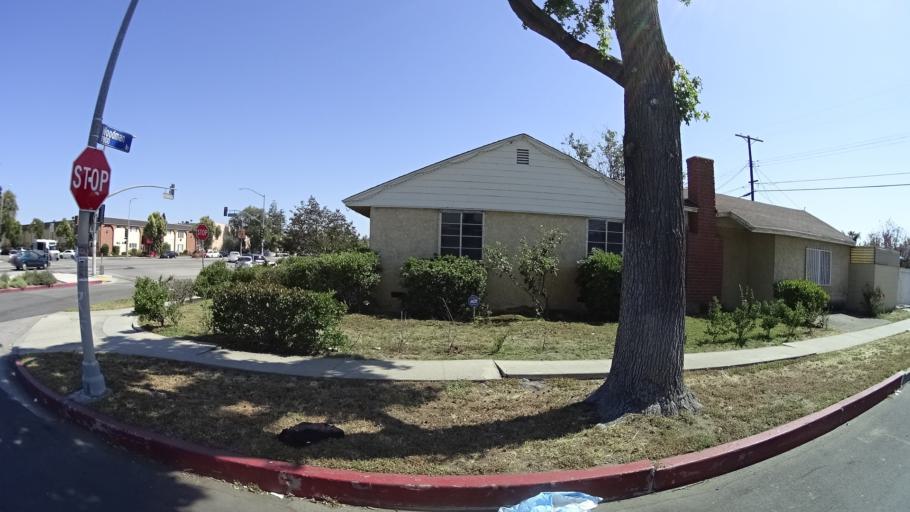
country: US
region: California
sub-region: Los Angeles County
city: Van Nuys
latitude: 34.2156
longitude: -118.4313
